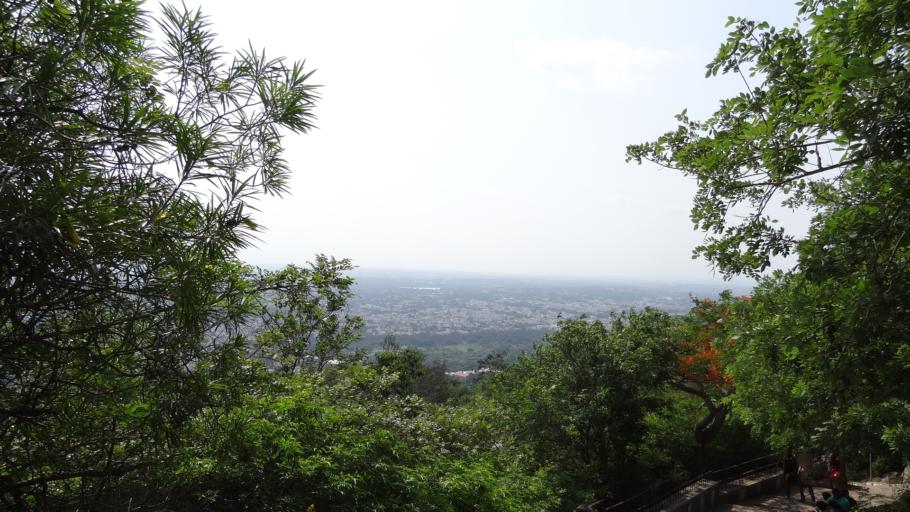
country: IN
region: Karnataka
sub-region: Mysore
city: Mysore
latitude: 12.2779
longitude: 76.6683
